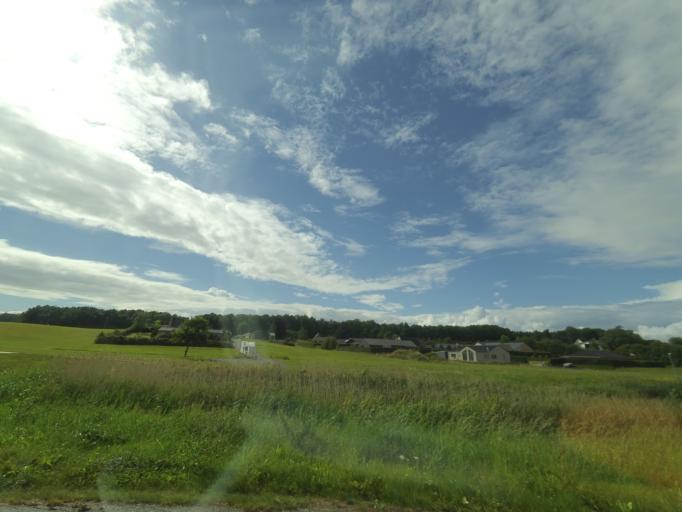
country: DK
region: South Denmark
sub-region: Nordfyns Kommune
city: Sonderso
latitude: 55.4494
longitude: 10.1856
